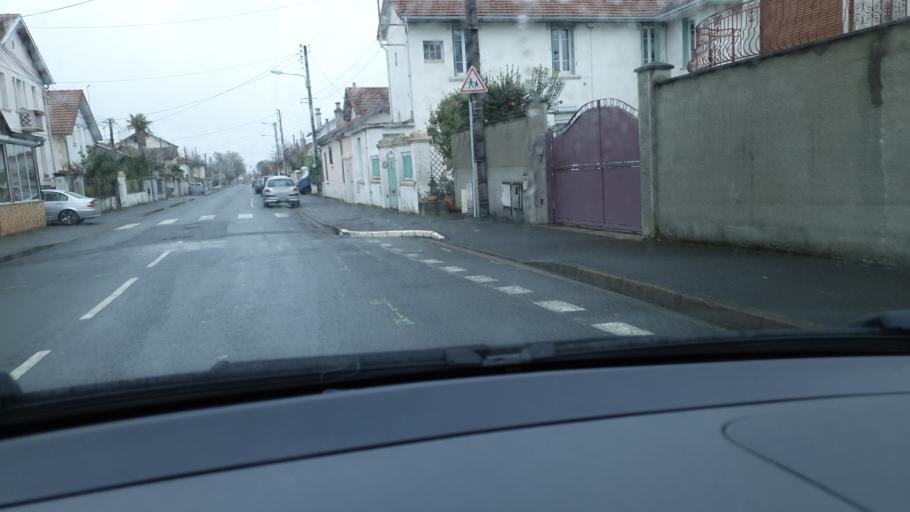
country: FR
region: Midi-Pyrenees
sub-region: Departement des Hautes-Pyrenees
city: Tarbes
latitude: 43.2372
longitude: 0.0514
